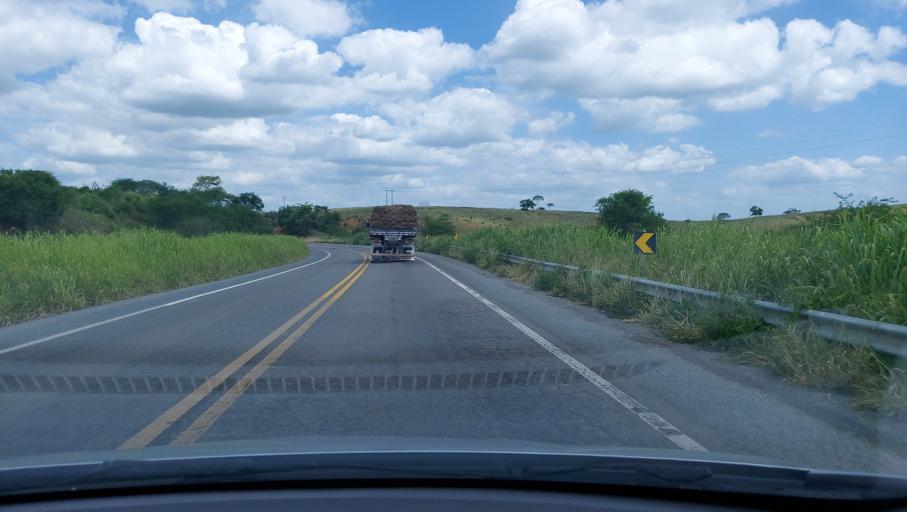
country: BR
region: Bahia
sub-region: Ruy Barbosa
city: Terra Nova
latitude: -12.4446
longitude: -40.7951
